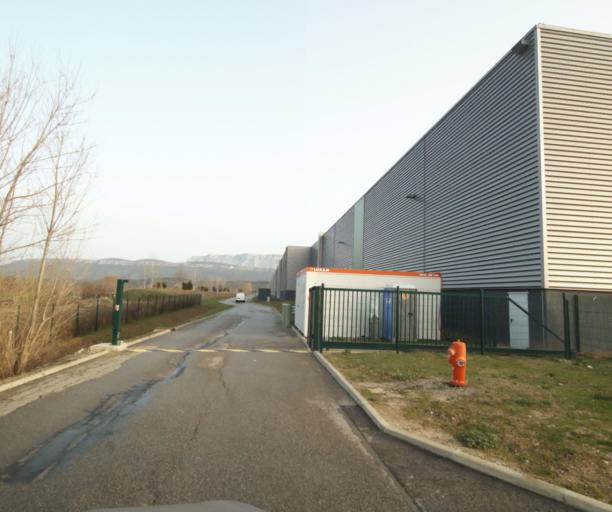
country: FR
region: Provence-Alpes-Cote d'Azur
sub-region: Departement des Bouches-du-Rhone
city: Rousset
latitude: 43.4656
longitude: 5.5981
